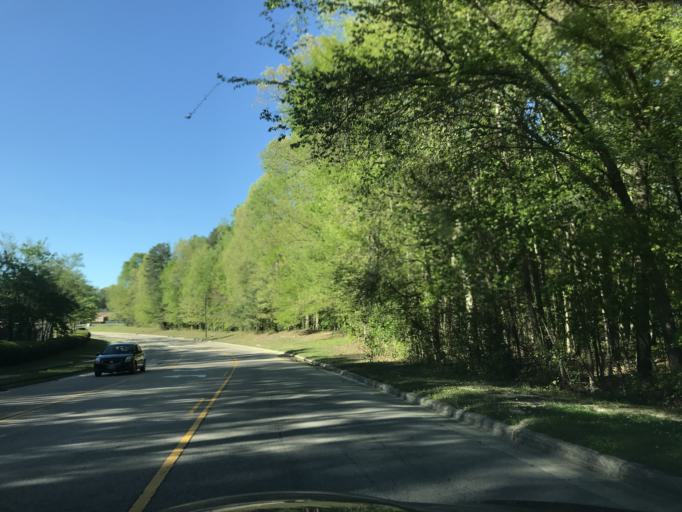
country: US
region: North Carolina
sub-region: Wake County
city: Knightdale
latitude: 35.7999
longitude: -78.5565
